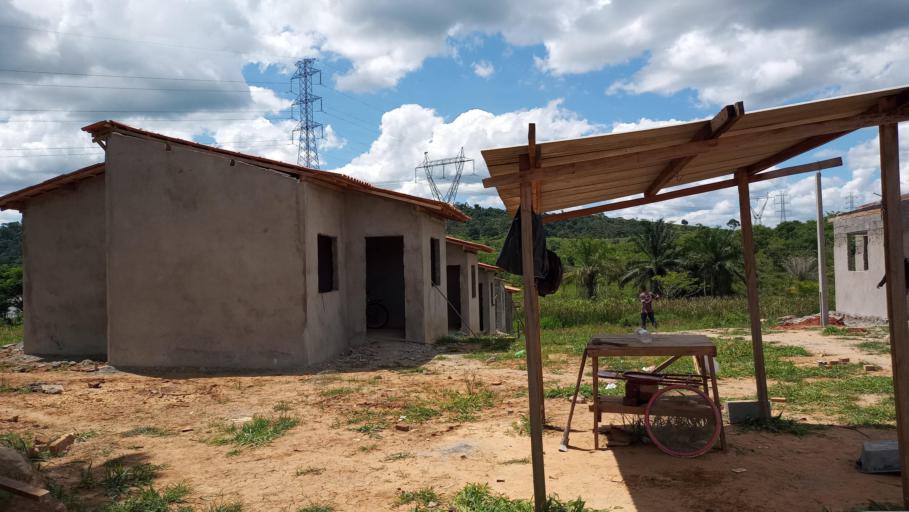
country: BR
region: Bahia
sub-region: Ubata
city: Ubata
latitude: -14.2095
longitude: -39.5368
